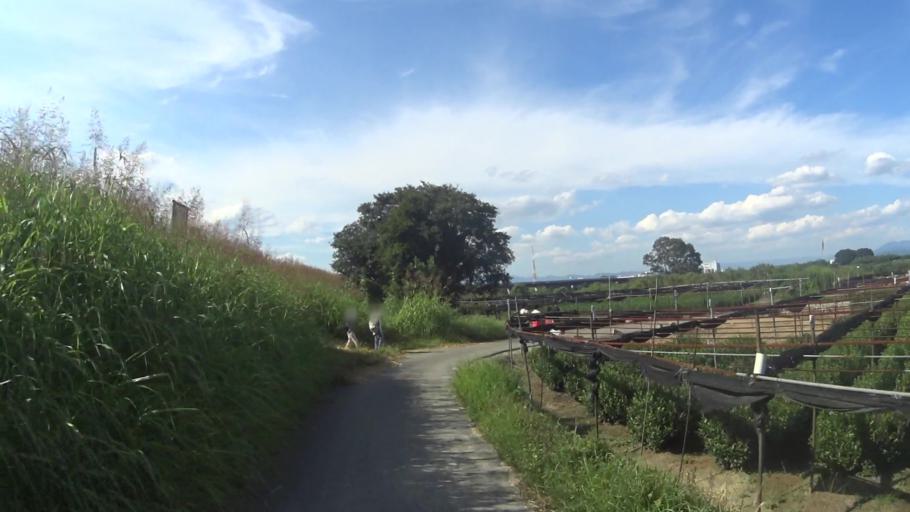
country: JP
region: Kyoto
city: Yawata
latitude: 34.8663
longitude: 135.7463
